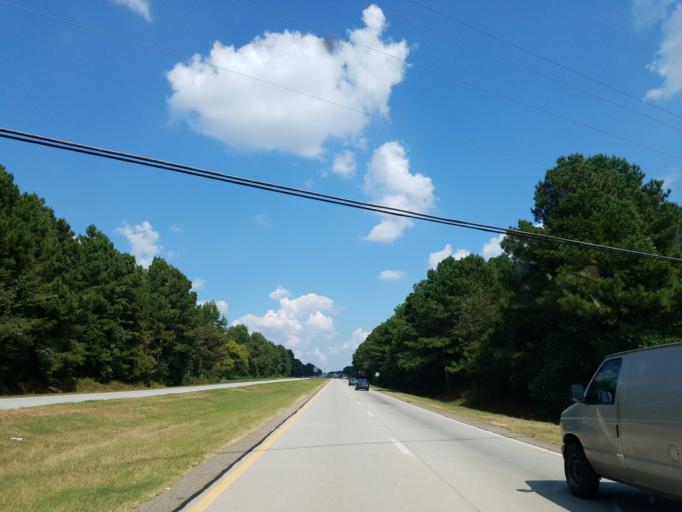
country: US
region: Georgia
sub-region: Clarke County
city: Athens
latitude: 33.9168
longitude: -83.3868
